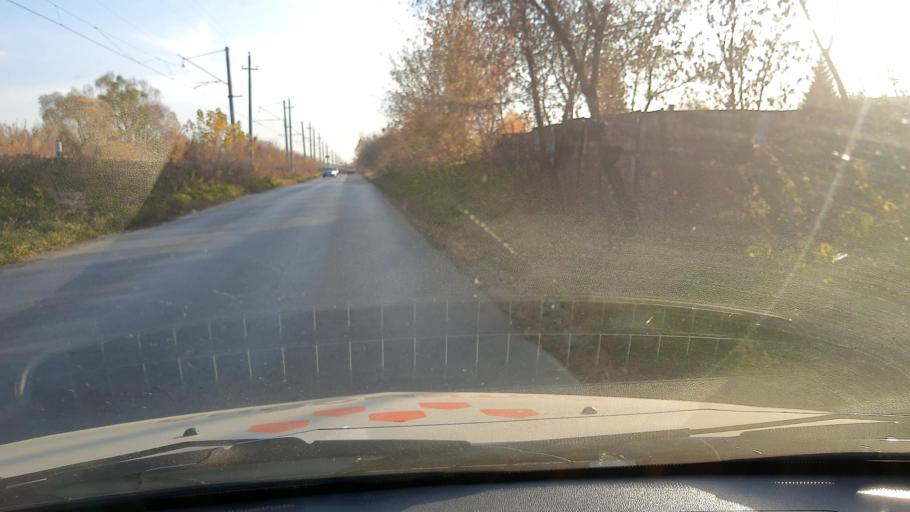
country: RU
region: Bashkortostan
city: Ufa
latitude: 54.8008
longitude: 56.1429
